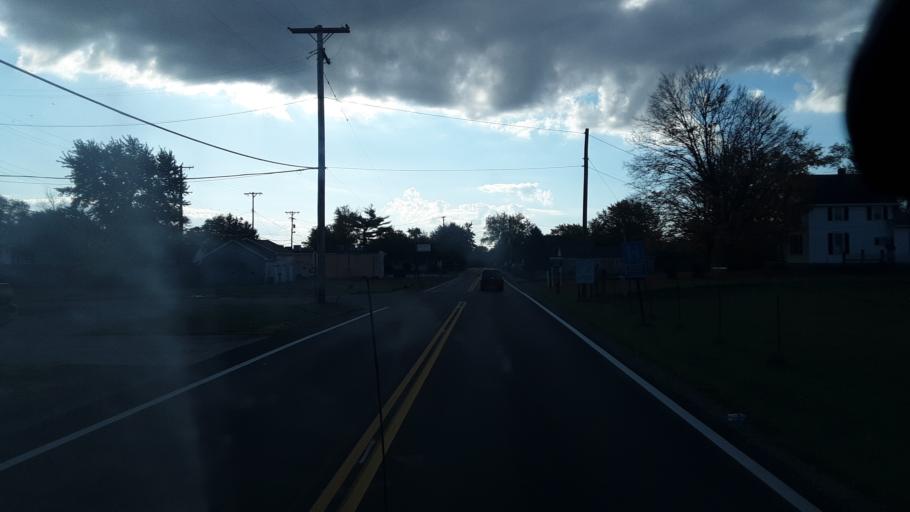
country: US
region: Ohio
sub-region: Fayette County
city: Washington Court House
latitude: 39.5476
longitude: -83.4485
